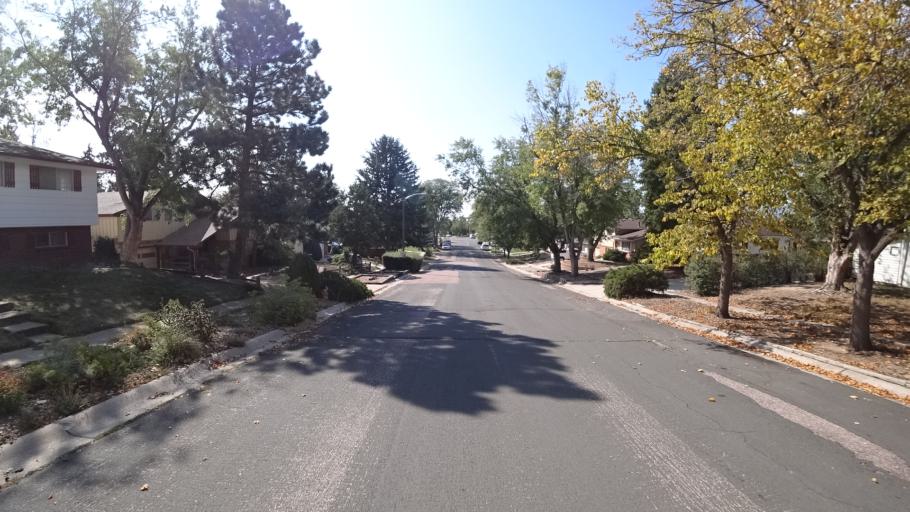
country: US
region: Colorado
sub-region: El Paso County
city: Cimarron Hills
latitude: 38.8630
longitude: -104.7629
